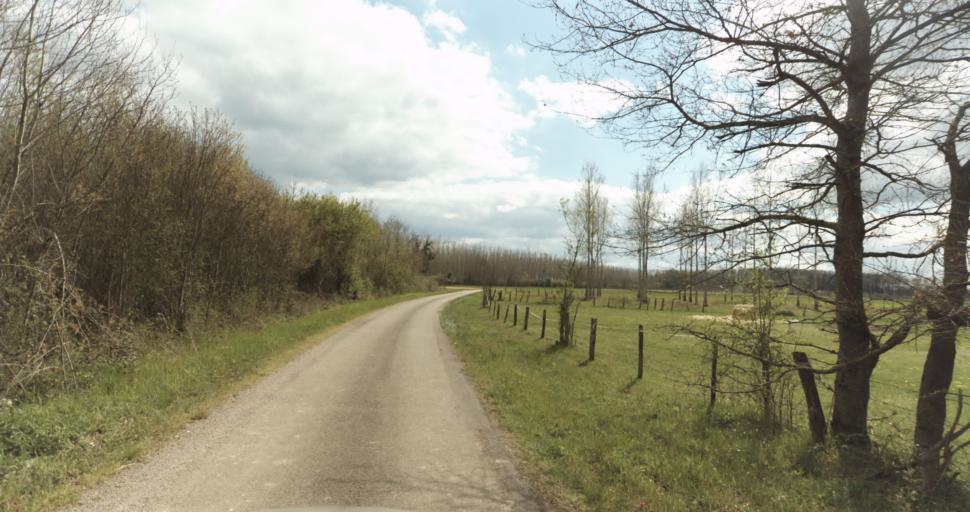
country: FR
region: Bourgogne
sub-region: Departement de la Cote-d'Or
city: Auxonne
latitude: 47.1646
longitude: 5.3959
